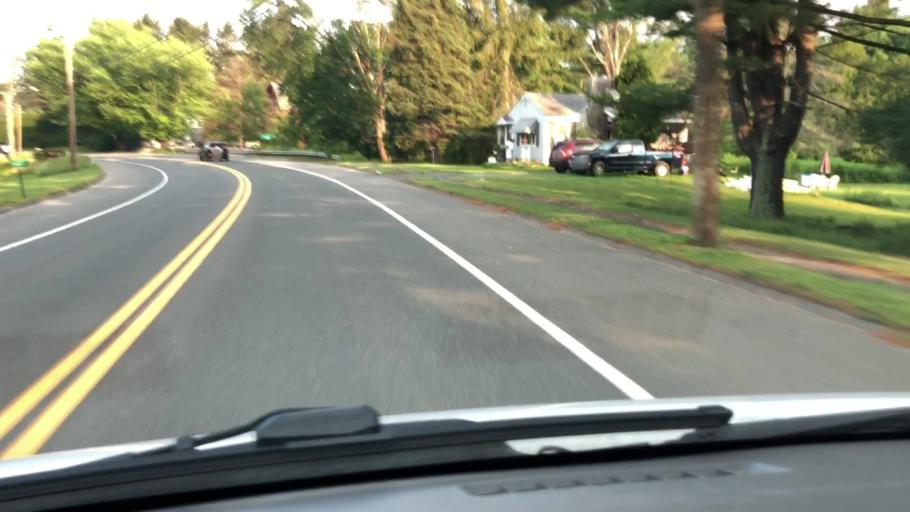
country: US
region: Massachusetts
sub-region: Berkshire County
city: Dalton
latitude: 42.4842
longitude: -73.1473
